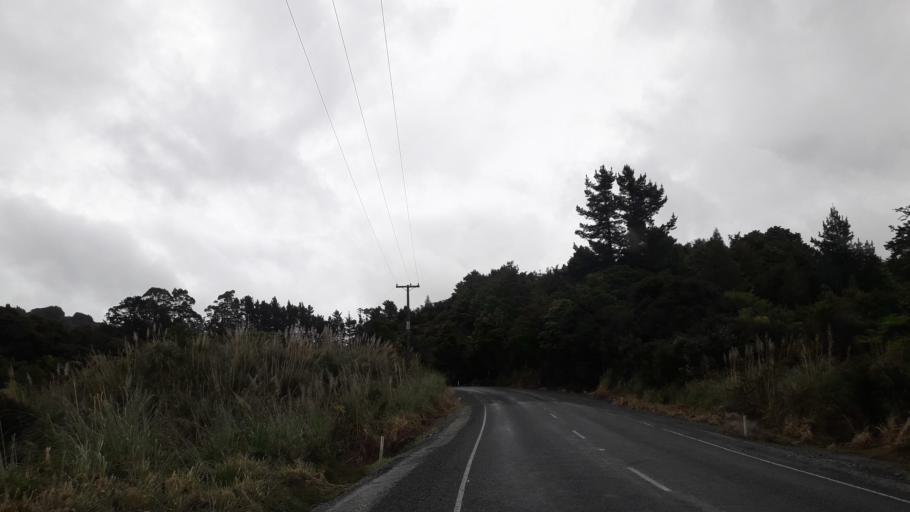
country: NZ
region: Northland
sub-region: Far North District
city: Kerikeri
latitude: -35.1153
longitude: 173.7540
